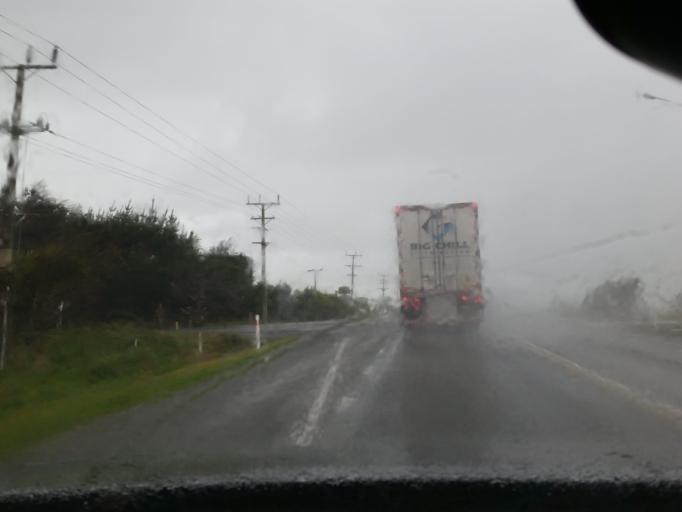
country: NZ
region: Southland
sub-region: Invercargill City
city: Bluff
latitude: -46.5477
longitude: 168.3007
